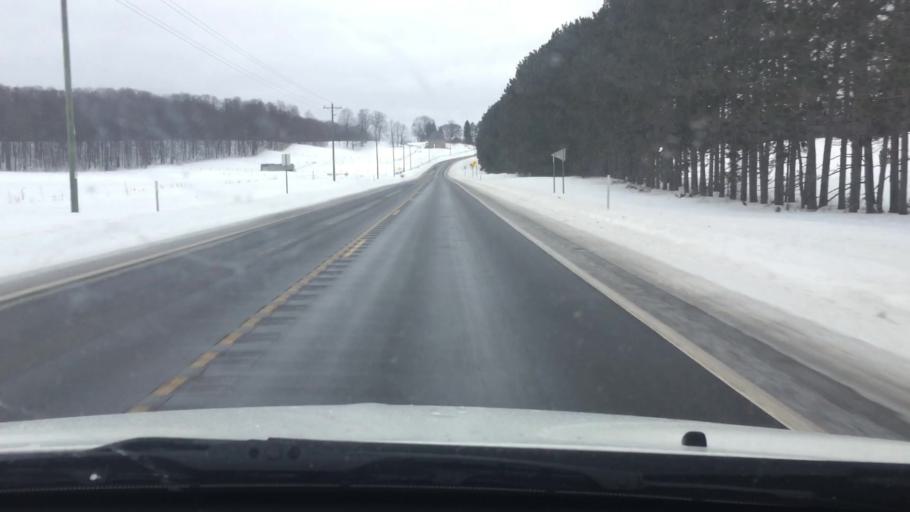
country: US
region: Michigan
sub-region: Charlevoix County
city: Boyne City
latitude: 45.0946
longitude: -84.9699
